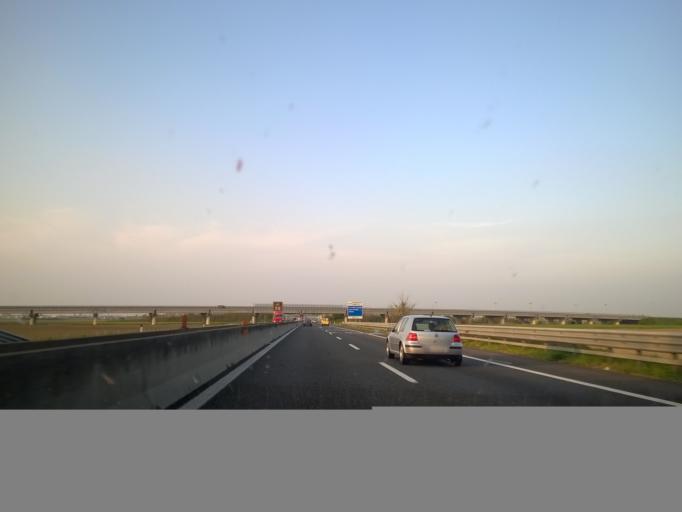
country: IT
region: Veneto
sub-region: Provincia di Rovigo
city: Villamarzana
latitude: 45.0193
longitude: 11.6911
